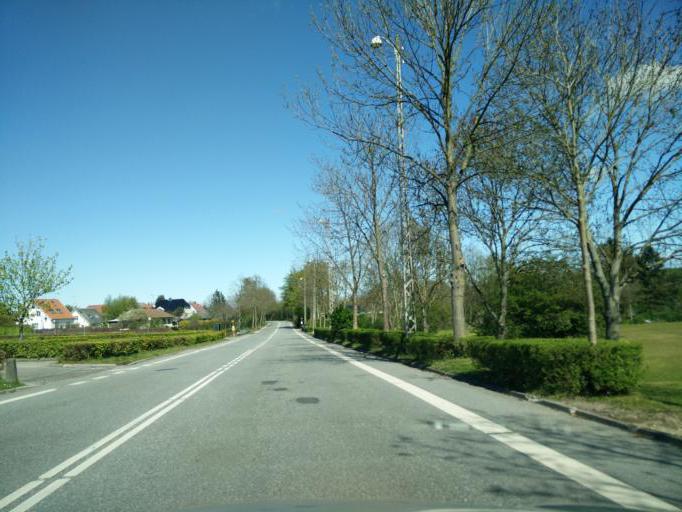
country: DK
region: Capital Region
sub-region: Gribskov Kommune
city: Helsinge
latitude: 56.0208
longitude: 12.2010
